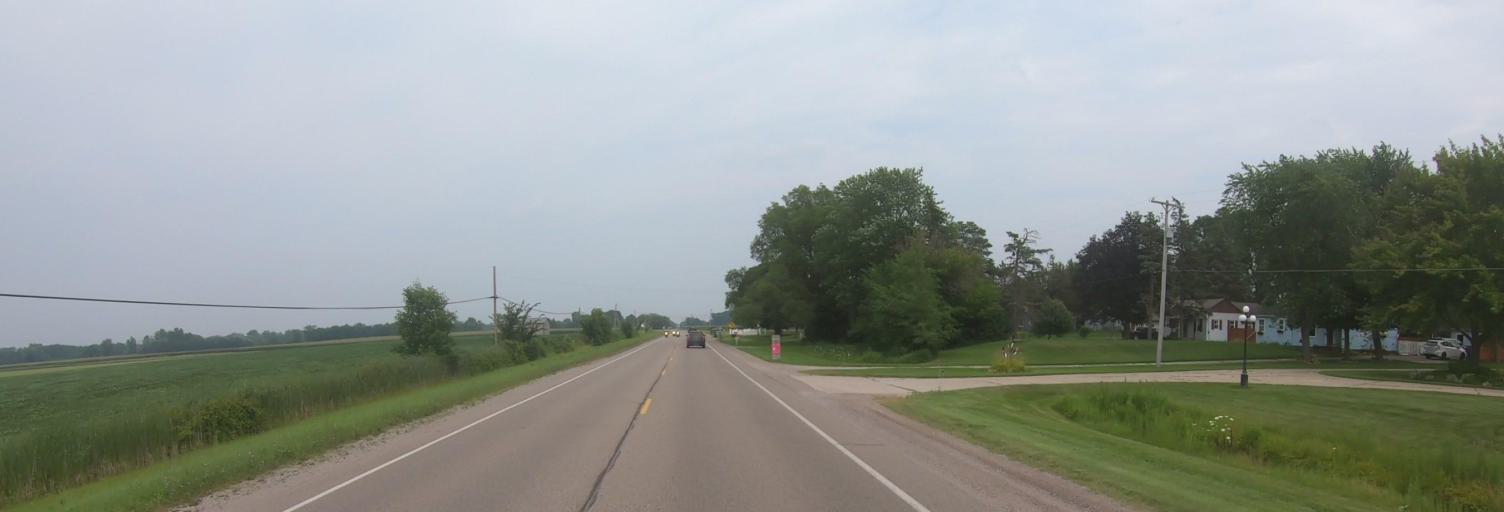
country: US
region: Michigan
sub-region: Shiawassee County
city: Durand
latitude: 42.9255
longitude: -83.9726
